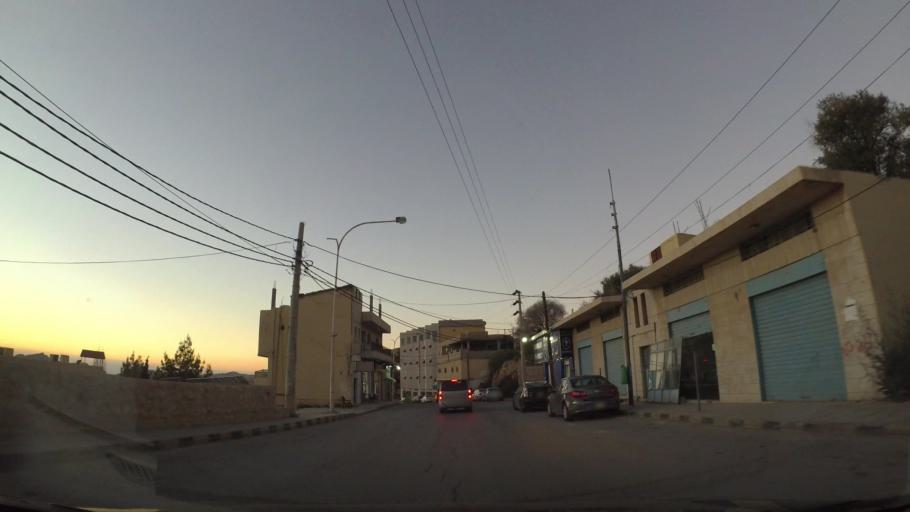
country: JO
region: Ma'an
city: Petra
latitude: 30.3197
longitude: 35.4813
